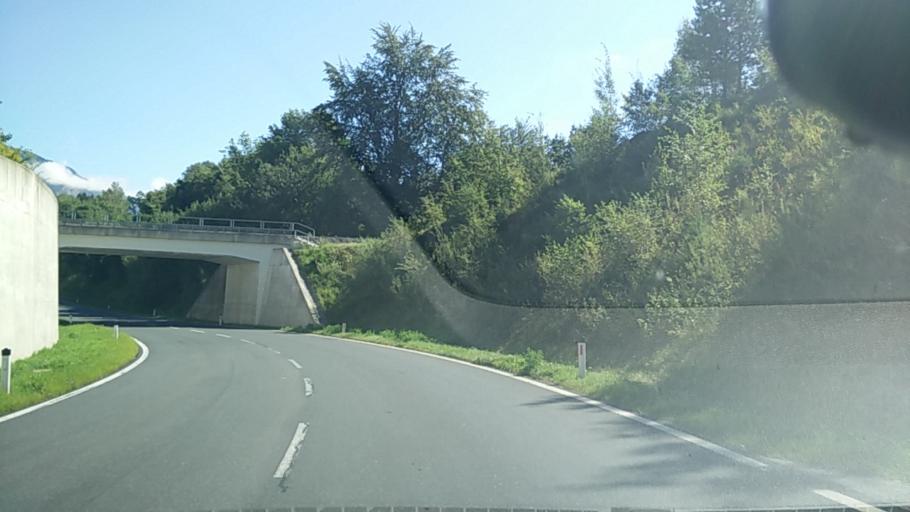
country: AT
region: Carinthia
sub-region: Politischer Bezirk Villach Land
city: Arnoldstein
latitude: 46.5540
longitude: 13.6963
